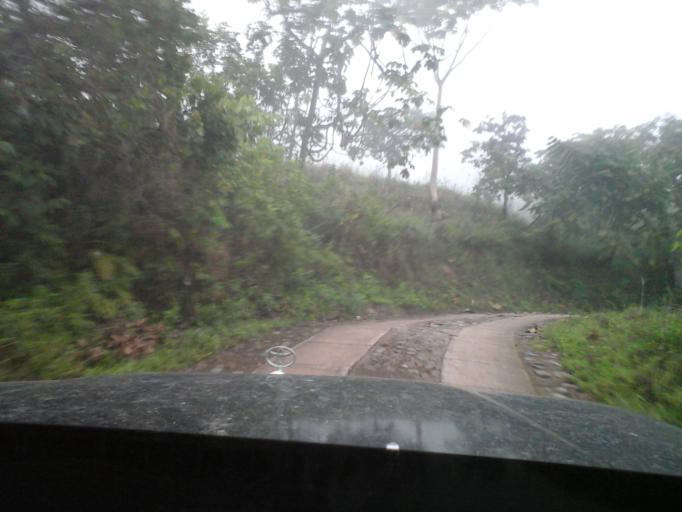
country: CO
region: Cesar
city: Agustin Codazzi
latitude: 9.9406
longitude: -73.1424
